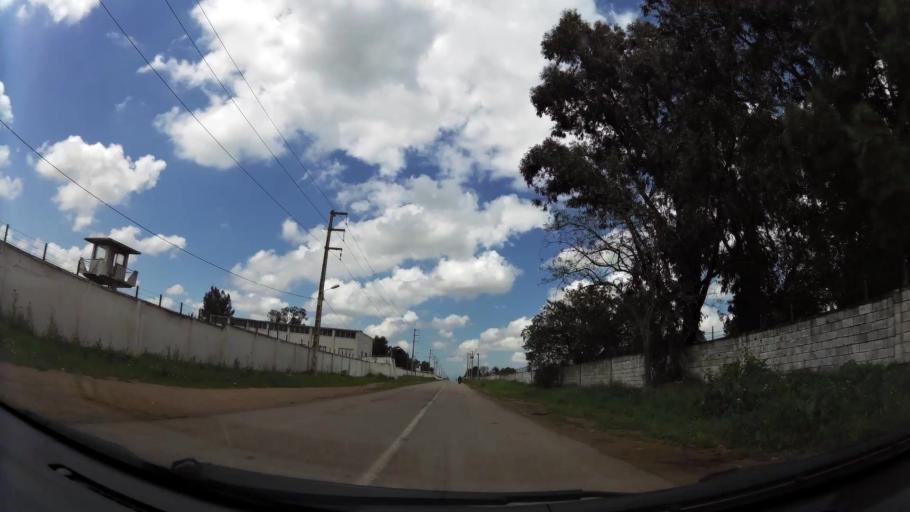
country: MA
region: Chaouia-Ouardigha
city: Nouaseur
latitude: 33.3872
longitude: -7.5760
